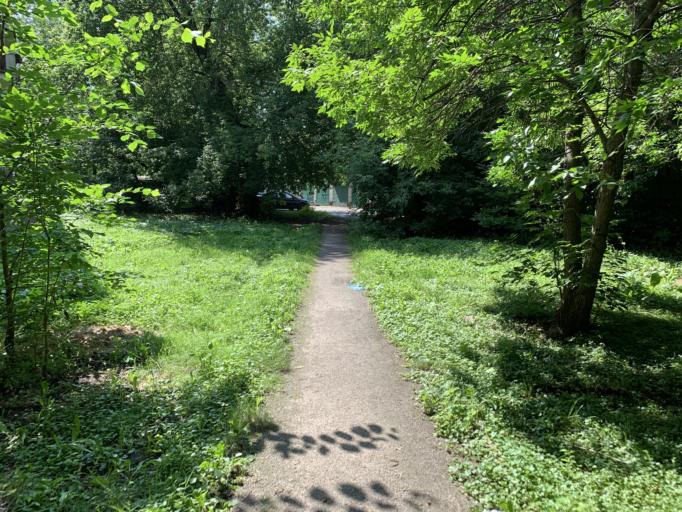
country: RU
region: Moscow
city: Vatutino
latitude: 55.8653
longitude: 37.6919
